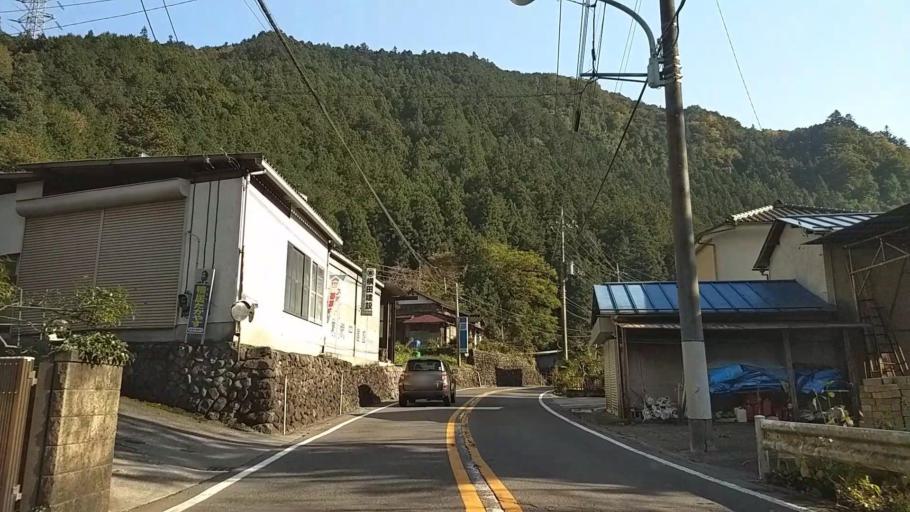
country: JP
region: Tokyo
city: Ome
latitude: 35.8073
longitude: 139.1767
